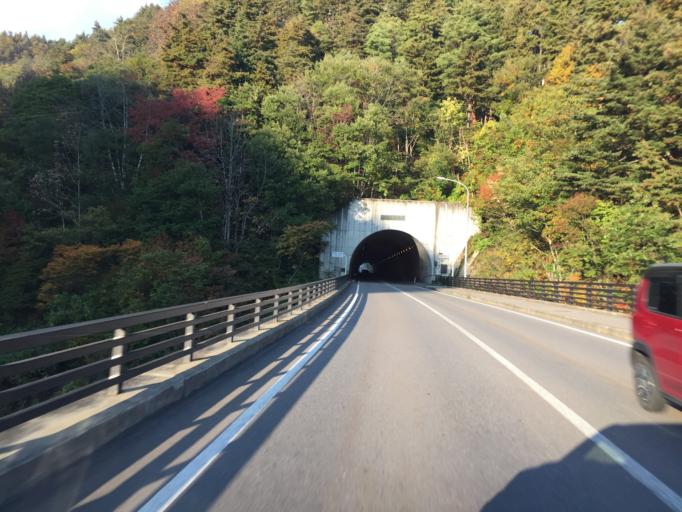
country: JP
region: Fukushima
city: Kitakata
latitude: 37.7508
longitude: 139.8966
